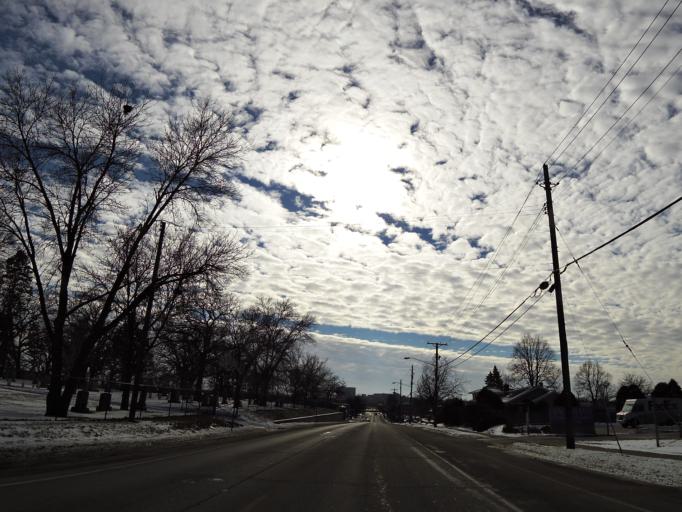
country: US
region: Minnesota
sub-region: Hennepin County
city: Richfield
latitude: 44.8960
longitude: -93.2883
